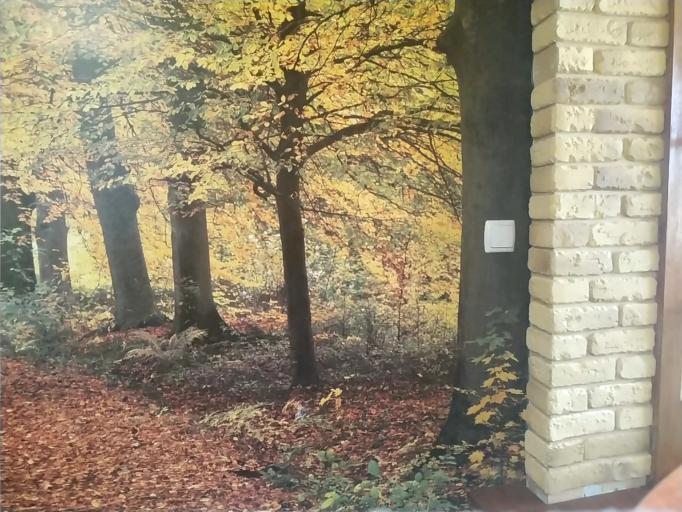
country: RU
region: Tverskaya
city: Krasnomayskiy
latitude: 57.6987
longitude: 34.4974
